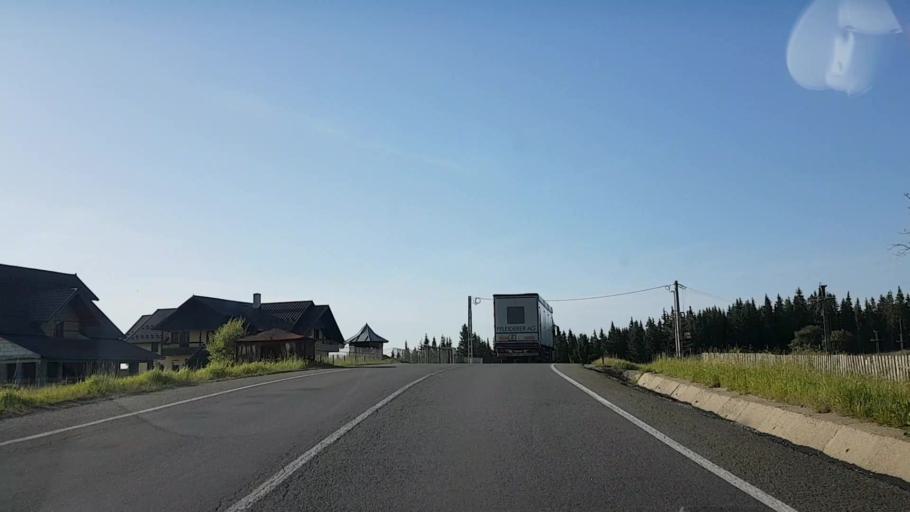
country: RO
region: Bistrita-Nasaud
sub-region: Comuna Lunca Ilvei
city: Lunca Ilvei
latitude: 47.2763
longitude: 25.0282
